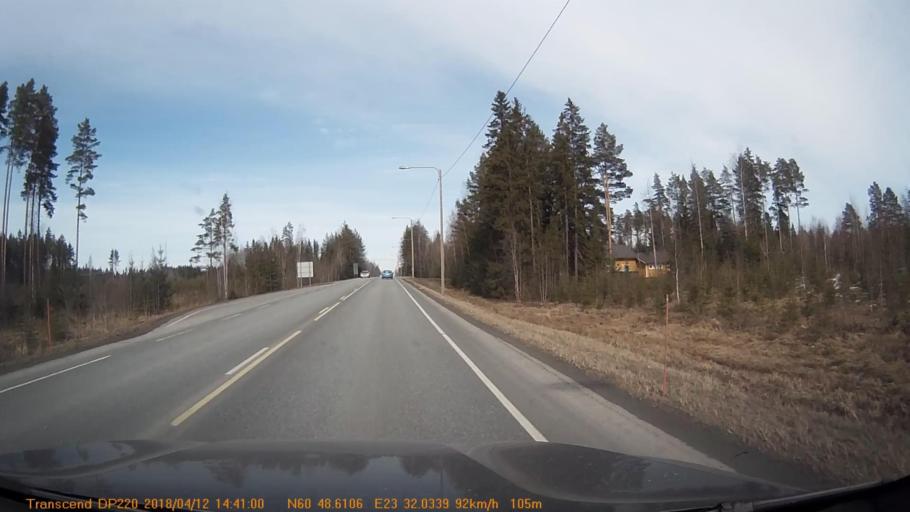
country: FI
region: Haeme
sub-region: Forssa
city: Jokioinen
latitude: 60.8104
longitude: 23.5343
